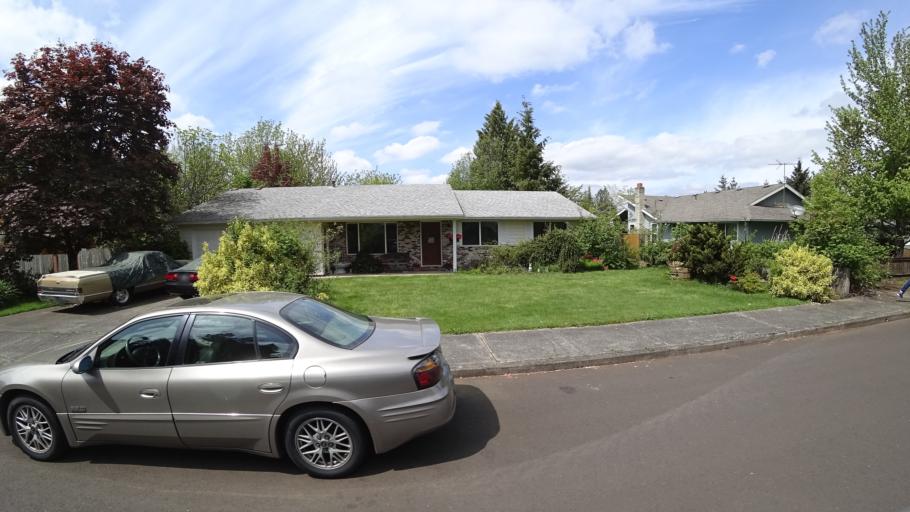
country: US
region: Oregon
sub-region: Washington County
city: Hillsboro
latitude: 45.5381
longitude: -122.9900
